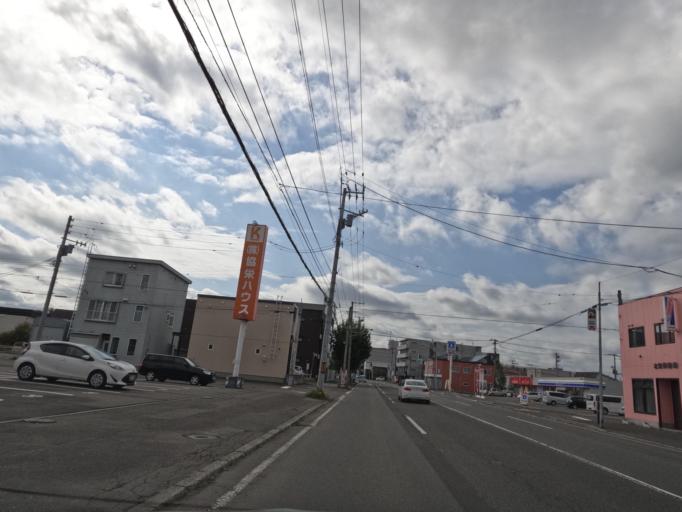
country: JP
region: Hokkaido
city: Chitose
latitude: 42.8190
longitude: 141.6524
